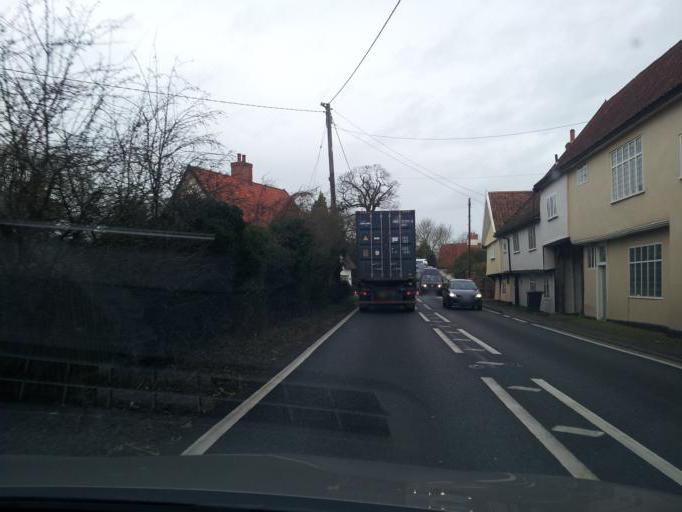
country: GB
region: England
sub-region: Suffolk
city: Debenham
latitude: 52.2595
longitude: 1.1019
